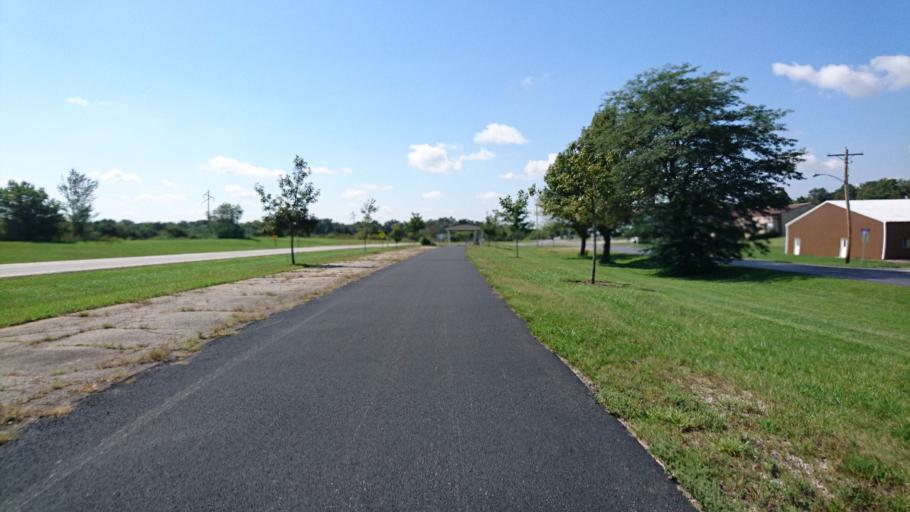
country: US
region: Illinois
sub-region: McLean County
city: Lexington
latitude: 40.6367
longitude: -88.7944
